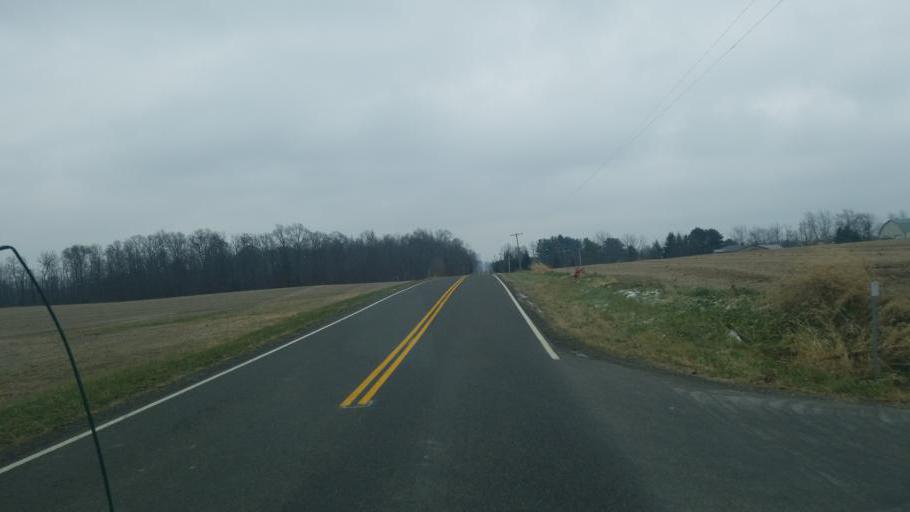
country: US
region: Ohio
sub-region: Medina County
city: Medina
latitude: 41.1359
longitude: -81.9624
